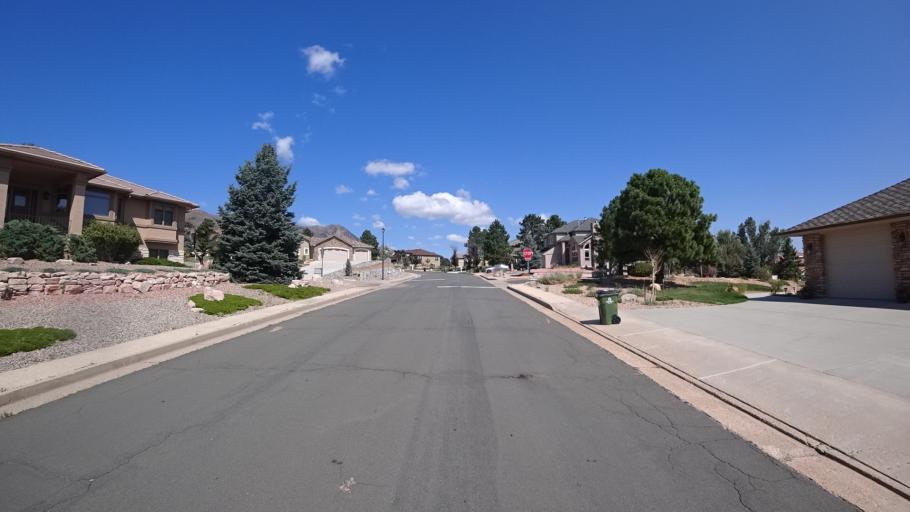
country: US
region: Colorado
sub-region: El Paso County
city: Manitou Springs
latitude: 38.9208
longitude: -104.8750
